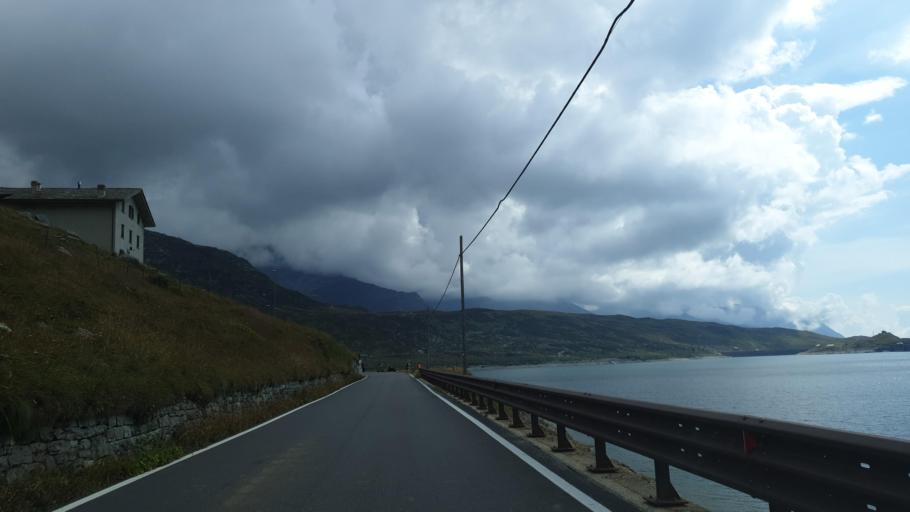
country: IT
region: Lombardy
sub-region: Provincia di Sondrio
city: Campodolcino
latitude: 46.4883
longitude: 9.3429
